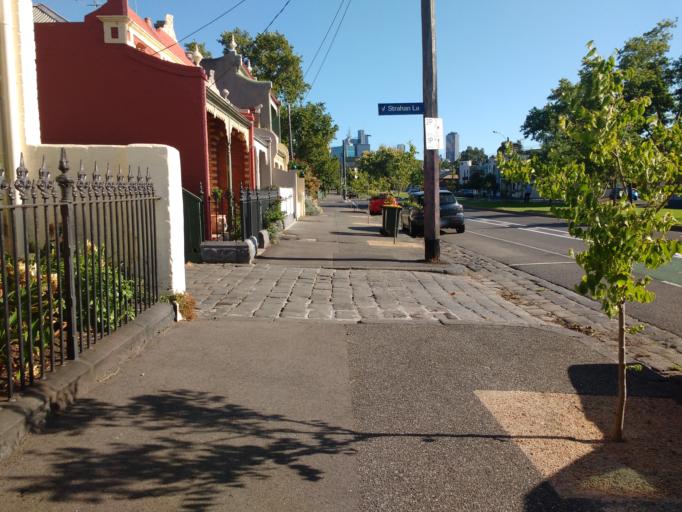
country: AU
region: Victoria
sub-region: Yarra
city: Fitzroy
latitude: -37.7946
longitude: 144.9736
